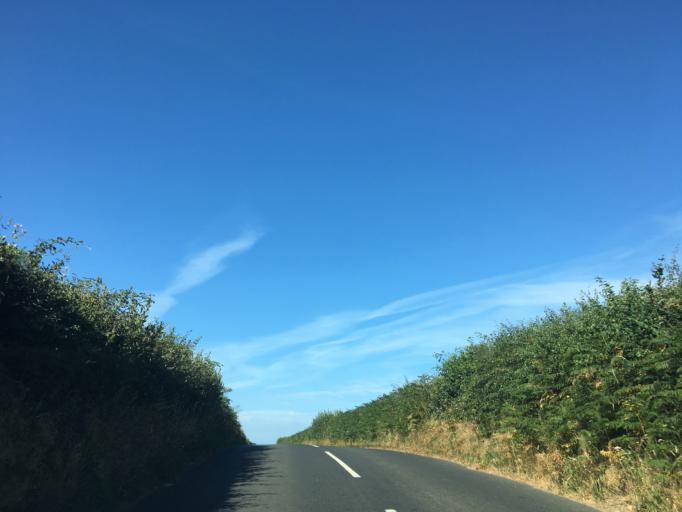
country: GB
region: England
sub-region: Isle of Wight
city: Chale
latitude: 50.6227
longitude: -1.2944
